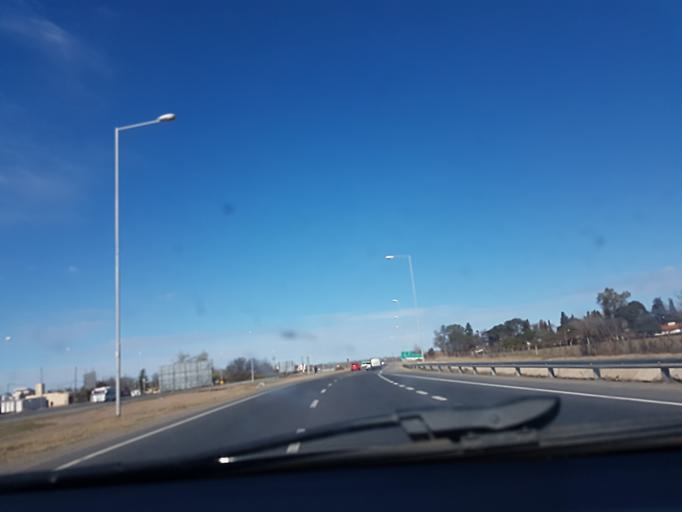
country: AR
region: Cordoba
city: La Calera
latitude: -31.3988
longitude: -64.2679
